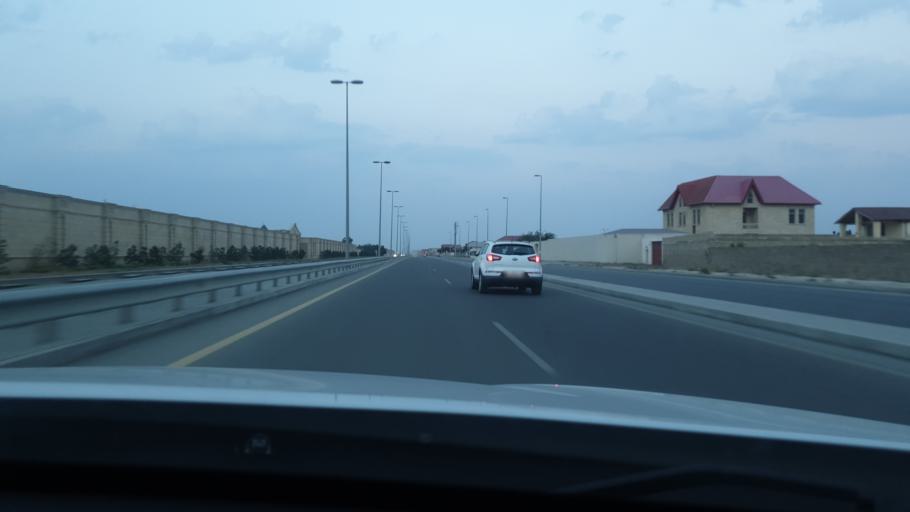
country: AZ
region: Baki
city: Bilajer
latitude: 40.5836
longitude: 50.0176
